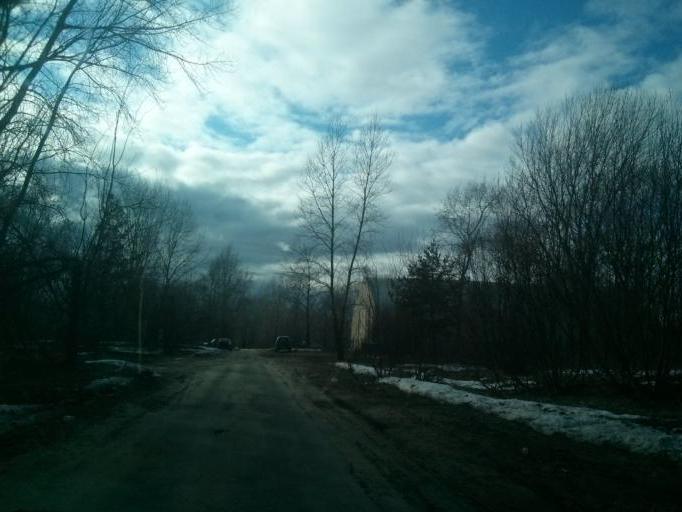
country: RU
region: Nizjnij Novgorod
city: Bor
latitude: 56.3292
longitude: 44.0569
